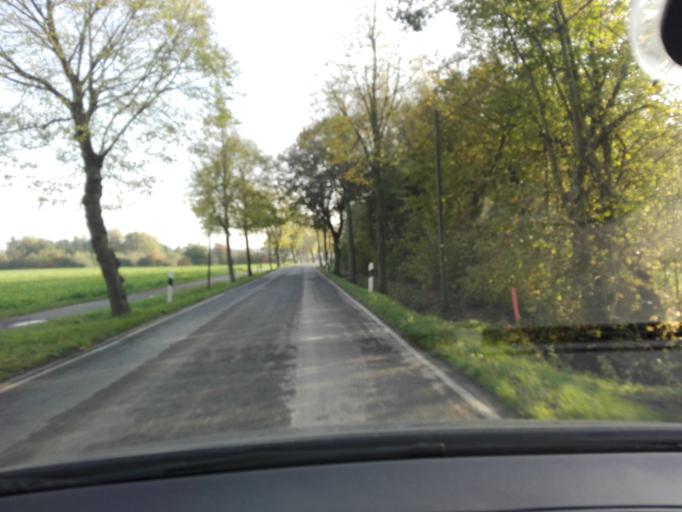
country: DE
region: North Rhine-Westphalia
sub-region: Regierungsbezirk Arnsberg
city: Unna
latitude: 51.5543
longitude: 7.7343
